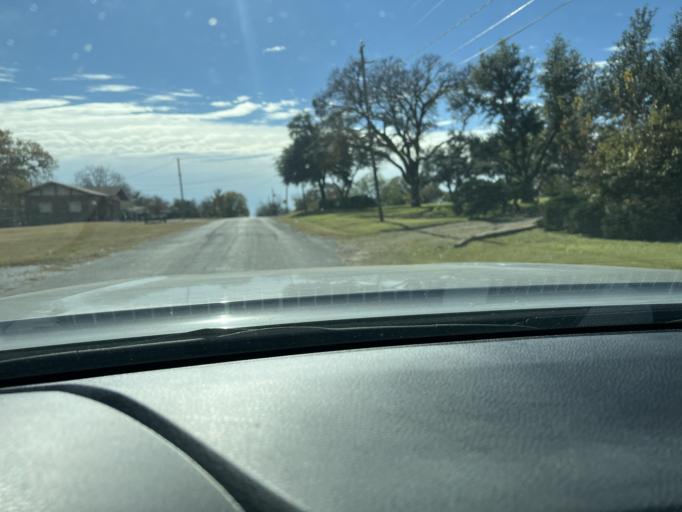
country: US
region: Texas
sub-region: Eastland County
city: Eastland
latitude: 32.3976
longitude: -98.8191
